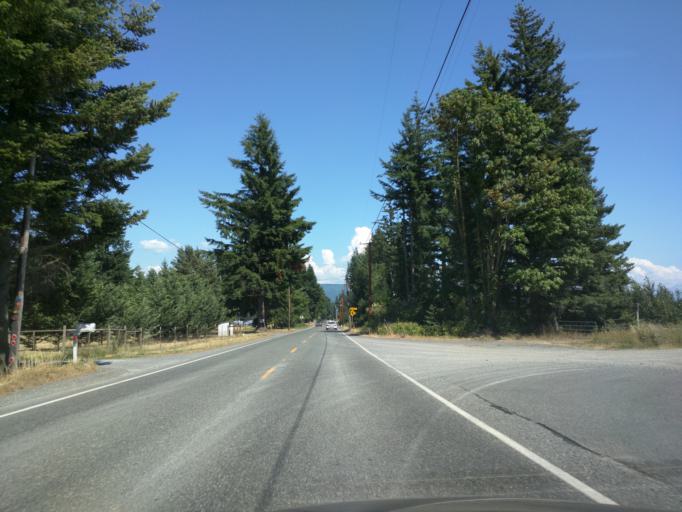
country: US
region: Washington
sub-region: Whatcom County
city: Everson
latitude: 48.8915
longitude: -122.3867
